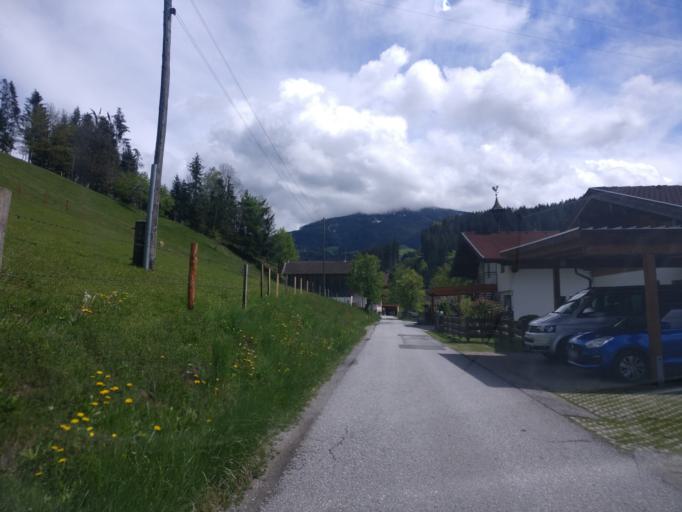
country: AT
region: Salzburg
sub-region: Politischer Bezirk Sankt Johann im Pongau
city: Bischofshofen
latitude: 47.4355
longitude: 13.2307
